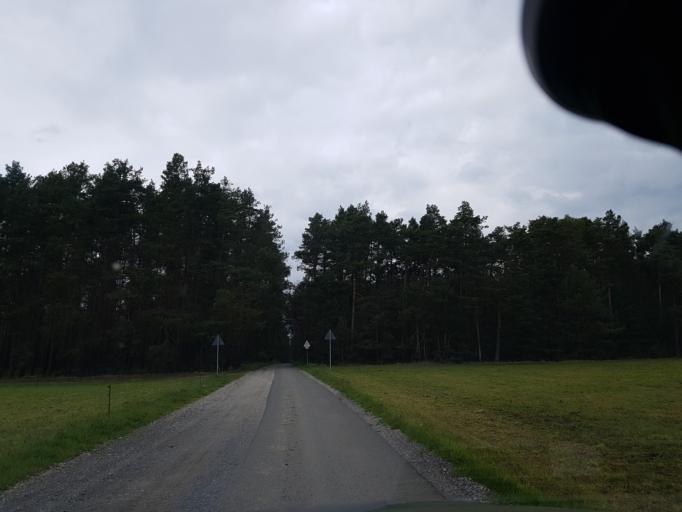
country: DE
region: Brandenburg
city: Crinitz
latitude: 51.6636
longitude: 13.7848
